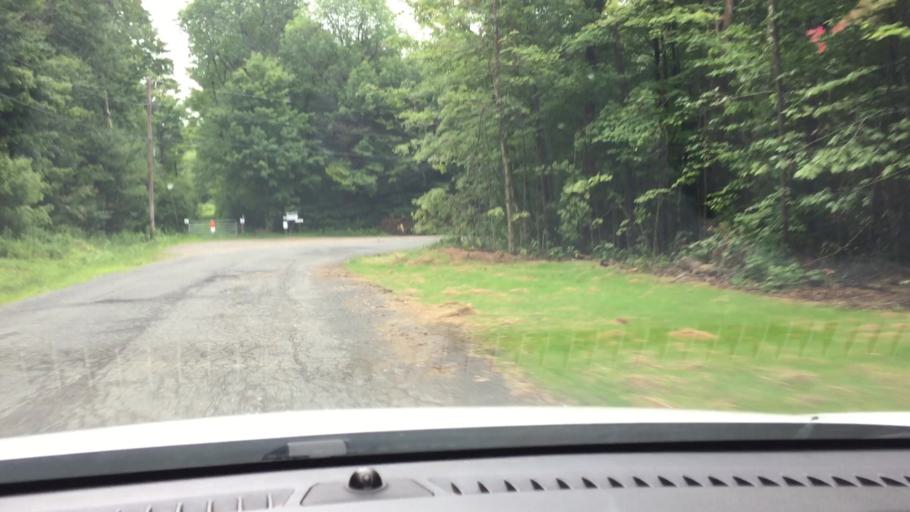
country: US
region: Massachusetts
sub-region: Berkshire County
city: Hinsdale
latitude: 42.4270
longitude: -73.0494
